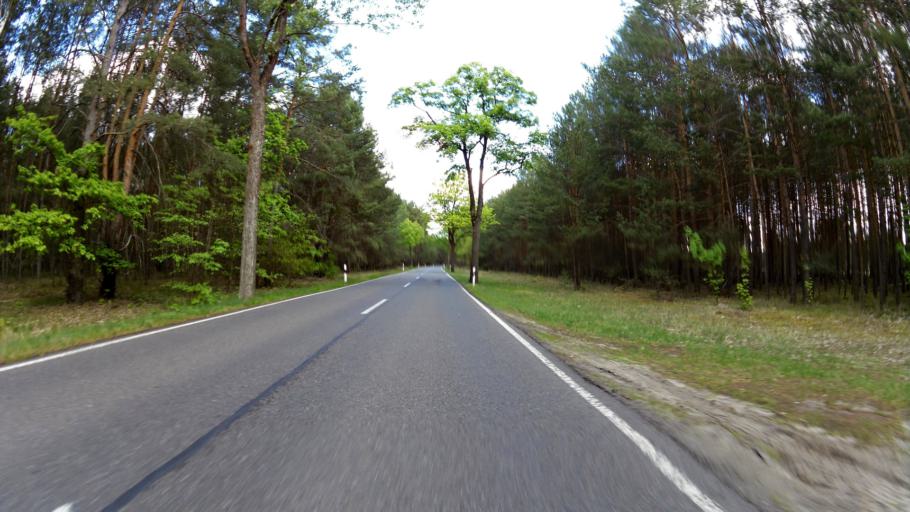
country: DE
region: Brandenburg
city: Wendisch Rietz
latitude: 52.1256
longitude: 13.9515
